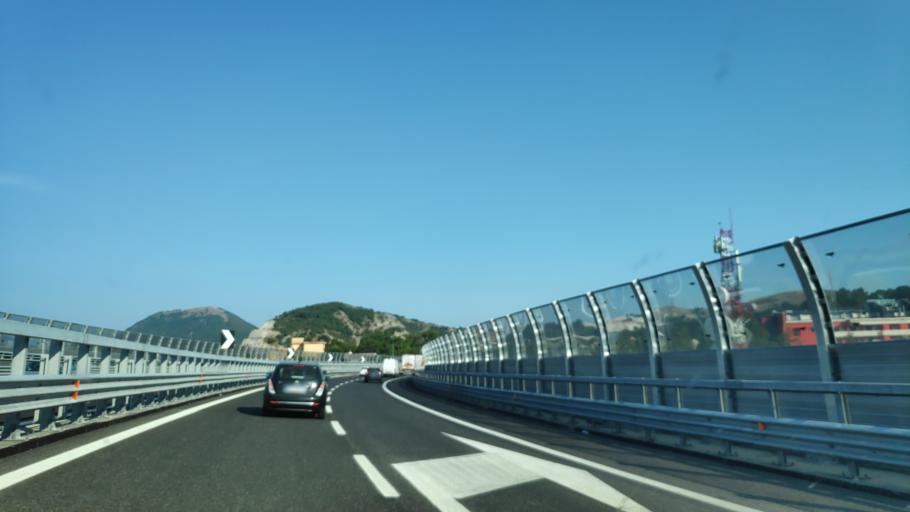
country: IT
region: Basilicate
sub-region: Provincia di Potenza
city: Lagonegro
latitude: 40.1311
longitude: 15.7632
